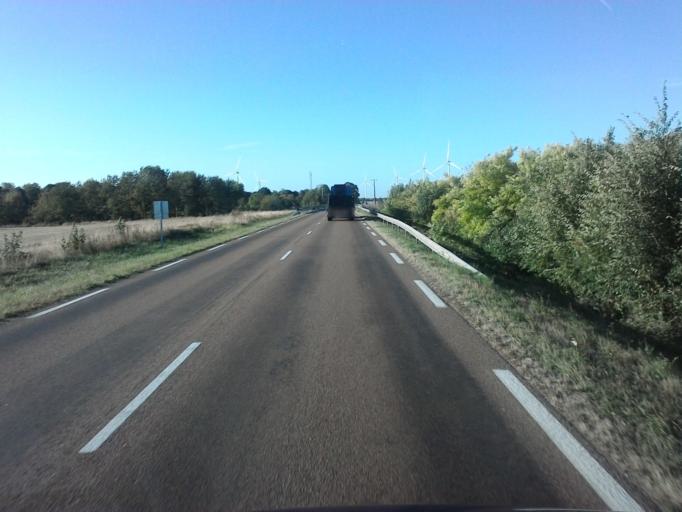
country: FR
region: Champagne-Ardenne
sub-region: Departement de l'Aube
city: Mailly-le-Camp
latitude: 48.6395
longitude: 4.1801
